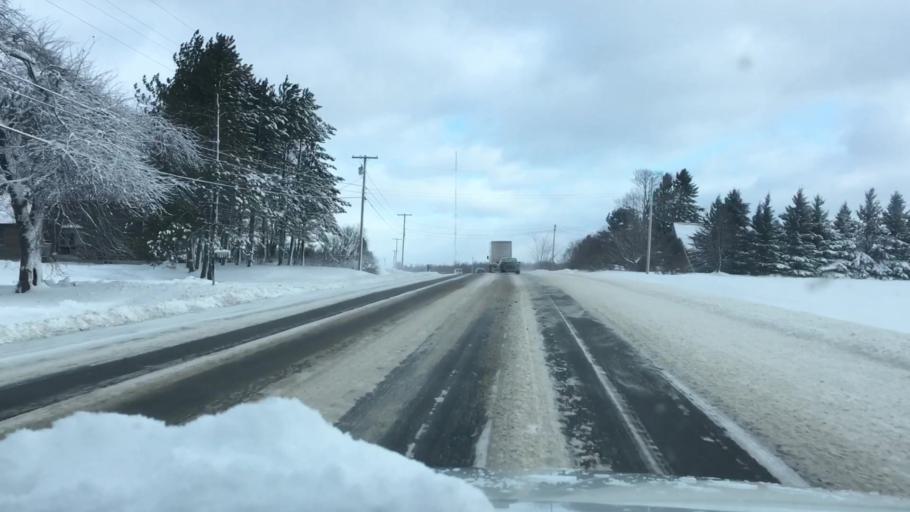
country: US
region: Maine
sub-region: Aroostook County
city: Presque Isle
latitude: 46.7569
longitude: -67.9908
